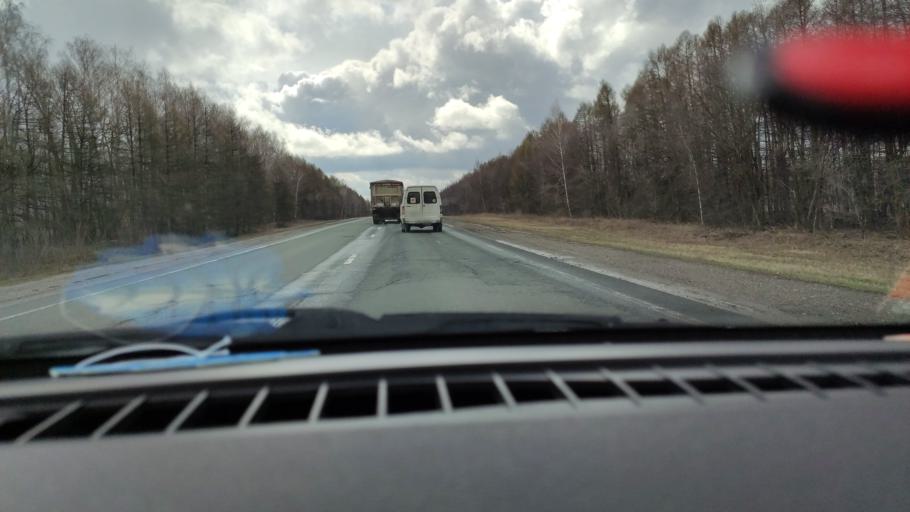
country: RU
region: Samara
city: Yelkhovka
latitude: 53.9730
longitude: 50.2659
